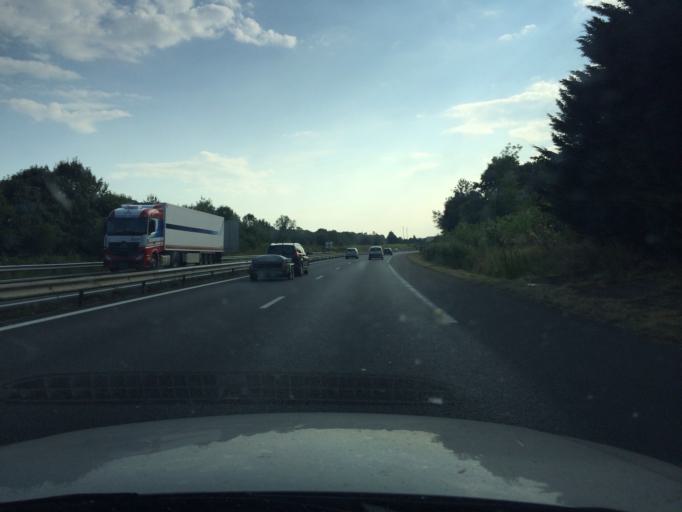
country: FR
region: Lower Normandy
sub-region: Departement du Calvados
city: Saint-Gatien-des-Bois
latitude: 49.2749
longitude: 0.1909
